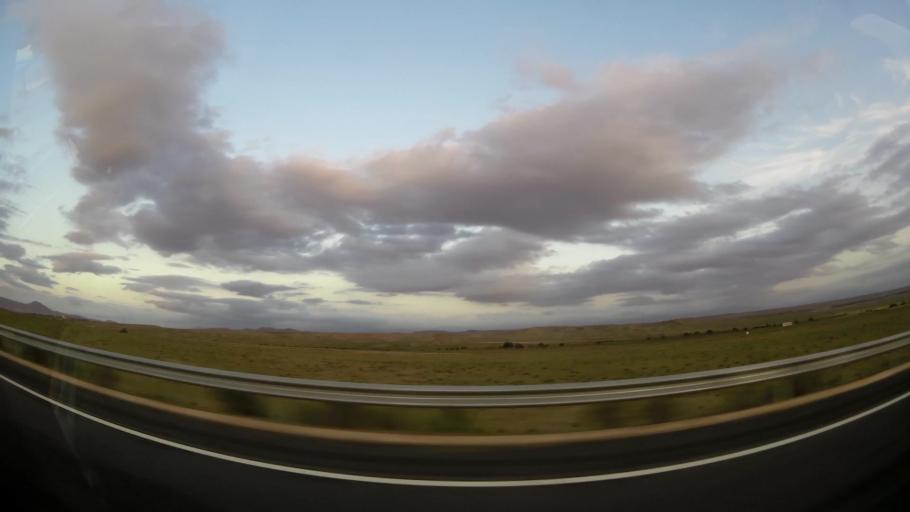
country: MA
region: Oriental
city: Taourirt
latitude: 34.5936
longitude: -2.7821
